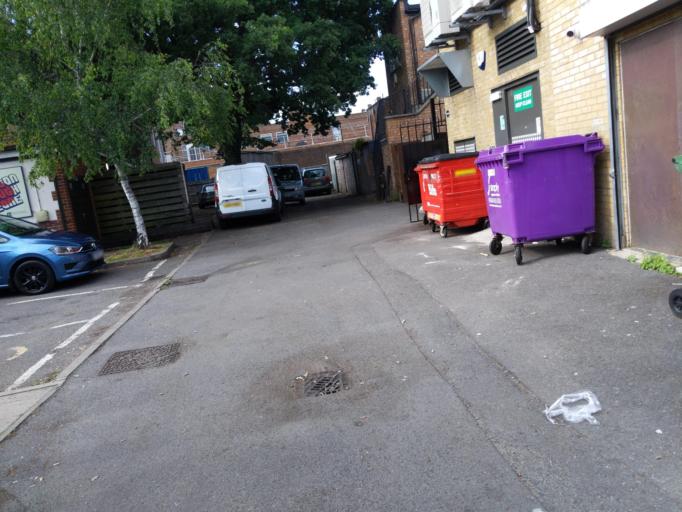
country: GB
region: England
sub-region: Greater London
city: Hounslow
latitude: 51.4504
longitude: -0.3583
